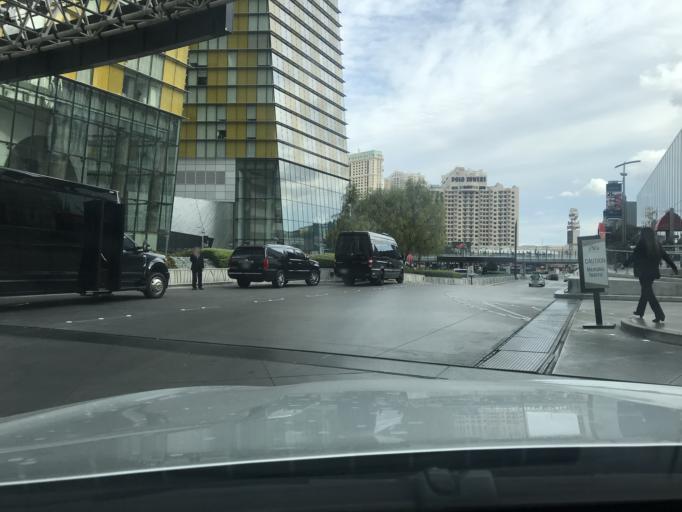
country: US
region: Nevada
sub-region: Clark County
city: Paradise
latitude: 36.1071
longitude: -115.1756
